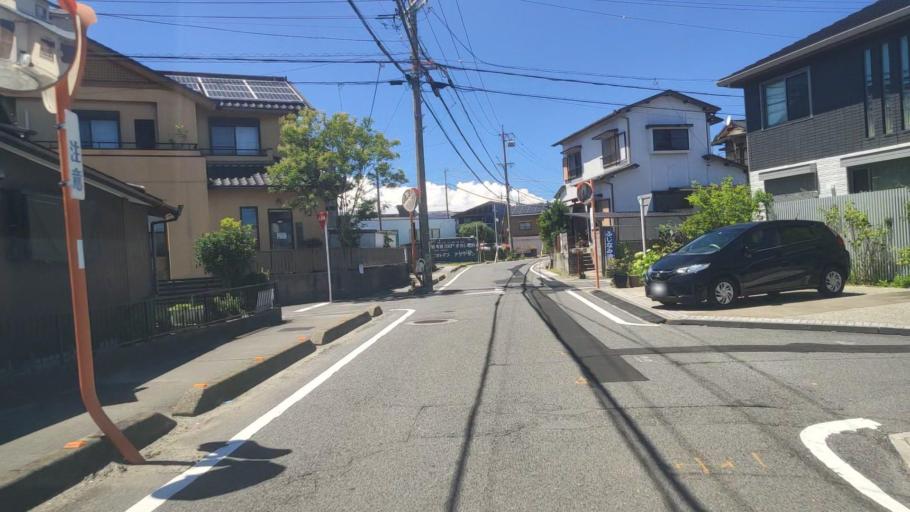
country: JP
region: Mie
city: Suzuka
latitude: 34.8537
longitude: 136.5916
